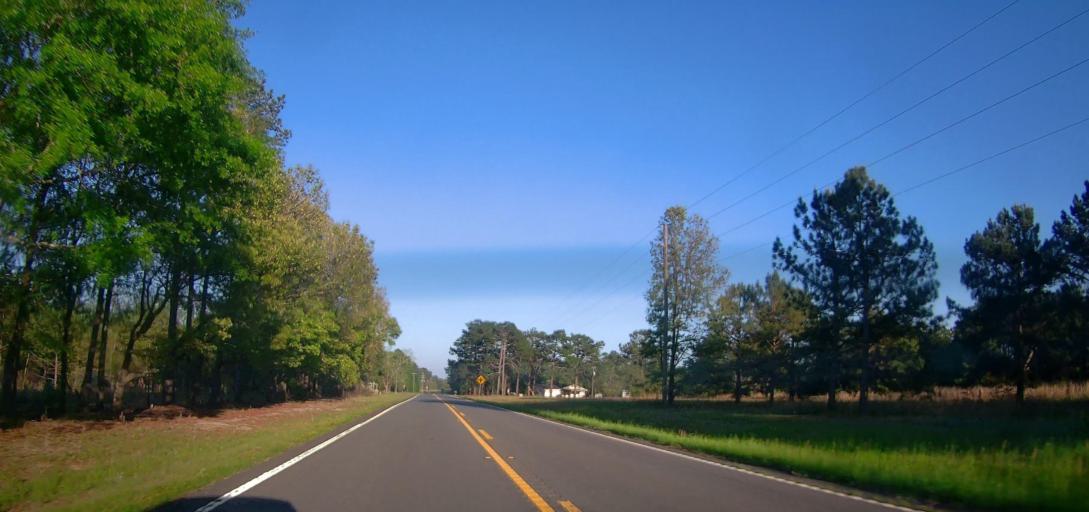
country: US
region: Georgia
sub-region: Schley County
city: Ellaville
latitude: 32.3322
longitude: -84.3447
